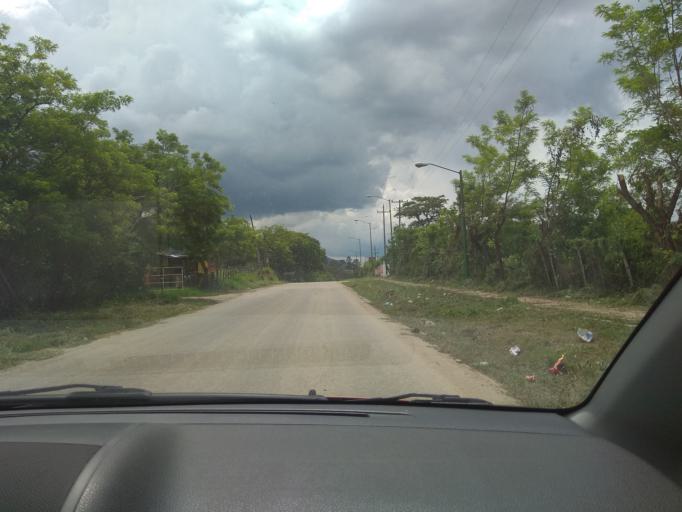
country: MX
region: Chiapas
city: Ocosingo
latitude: 16.8967
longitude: -92.0747
